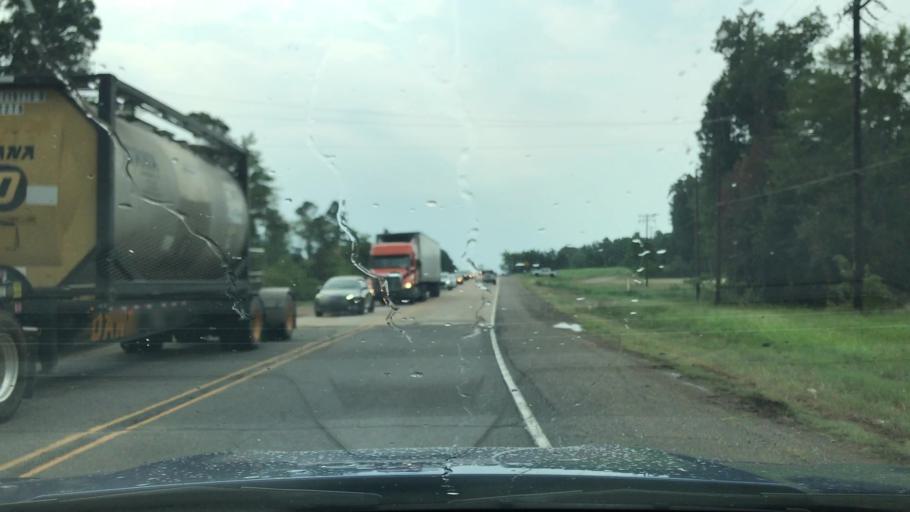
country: US
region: Louisiana
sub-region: Caddo Parish
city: Greenwood
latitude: 32.4485
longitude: -94.0098
